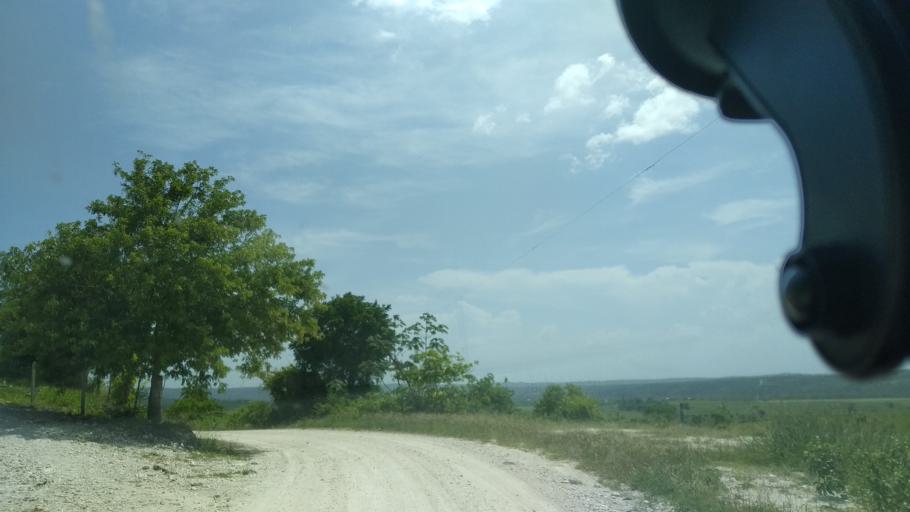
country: BZ
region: Cayo
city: San Ignacio
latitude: 17.2966
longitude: -89.0629
